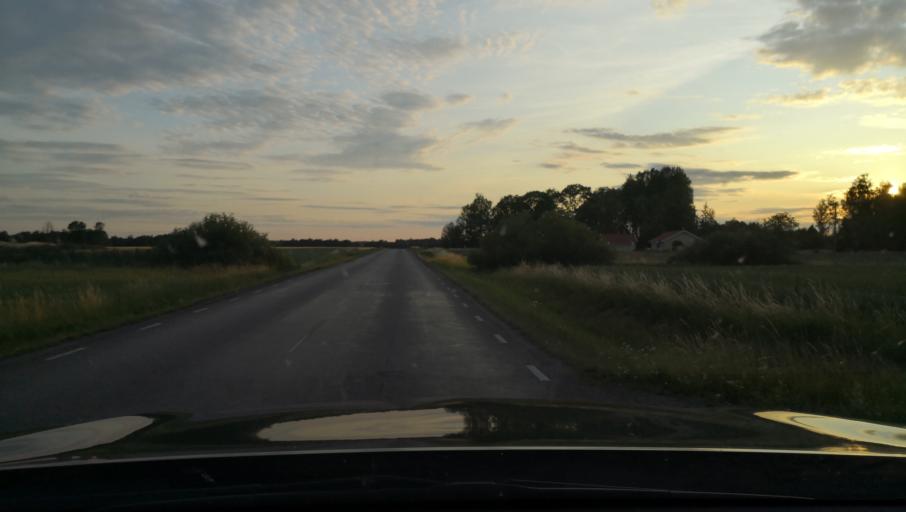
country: SE
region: Uppsala
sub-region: Uppsala Kommun
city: Vattholma
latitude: 60.0224
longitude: 17.6920
